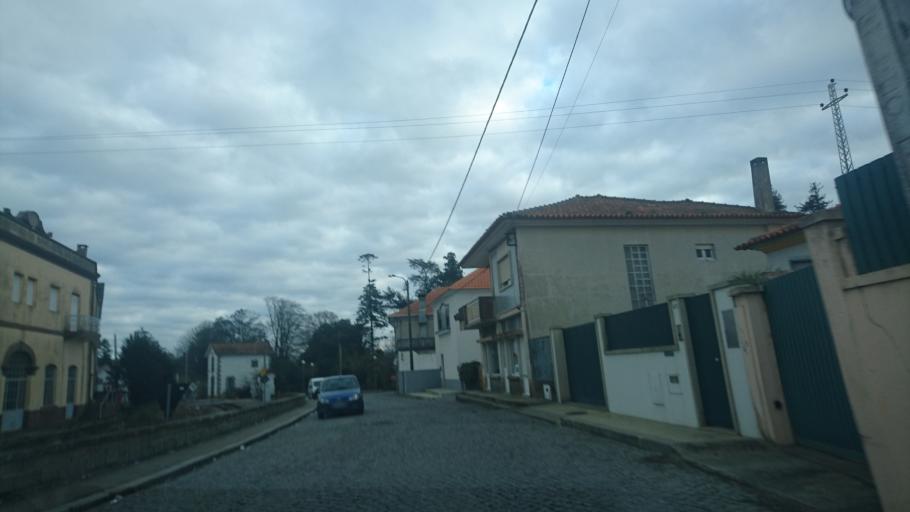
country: PT
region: Aveiro
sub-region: Santa Maria da Feira
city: Pacos de Brandao
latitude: 40.9725
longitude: -8.5856
